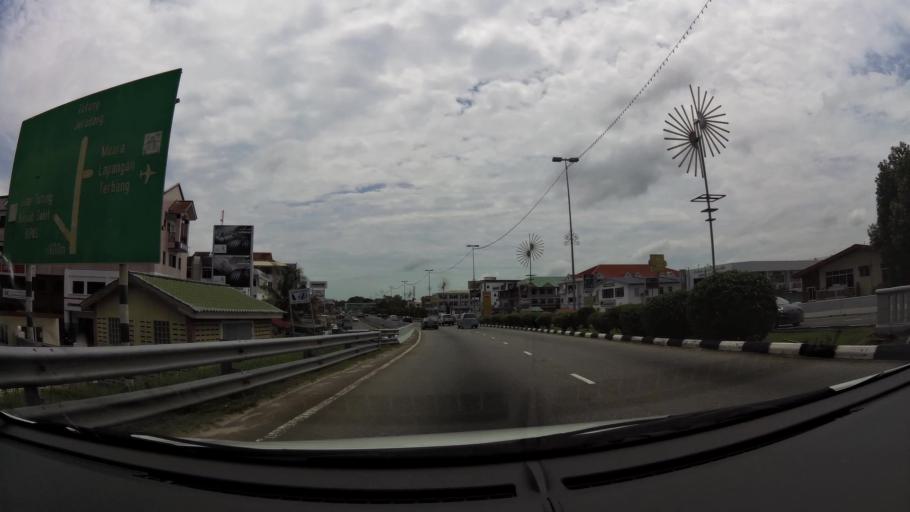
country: BN
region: Brunei and Muara
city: Bandar Seri Begawan
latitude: 4.9087
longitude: 114.9266
